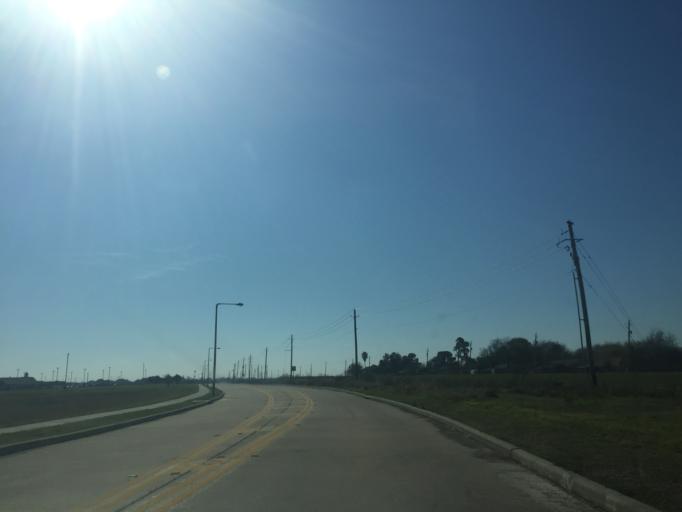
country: US
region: Texas
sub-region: Galveston County
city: Kemah
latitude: 29.5110
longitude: -95.0287
